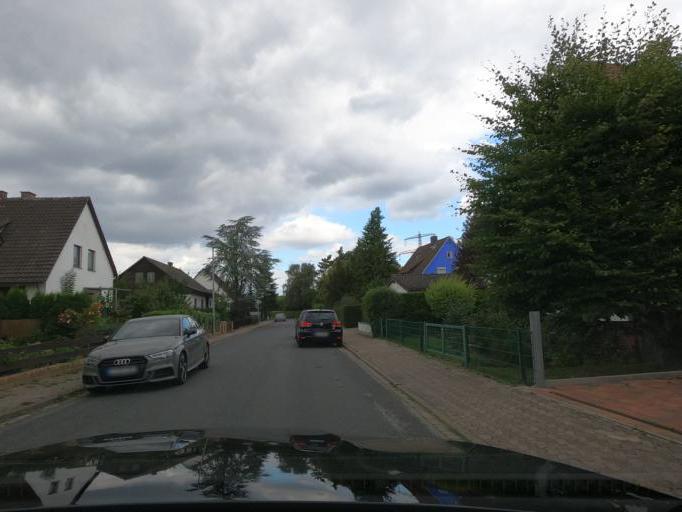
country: DE
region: Lower Saxony
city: Lehrte
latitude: 52.3689
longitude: 9.9057
